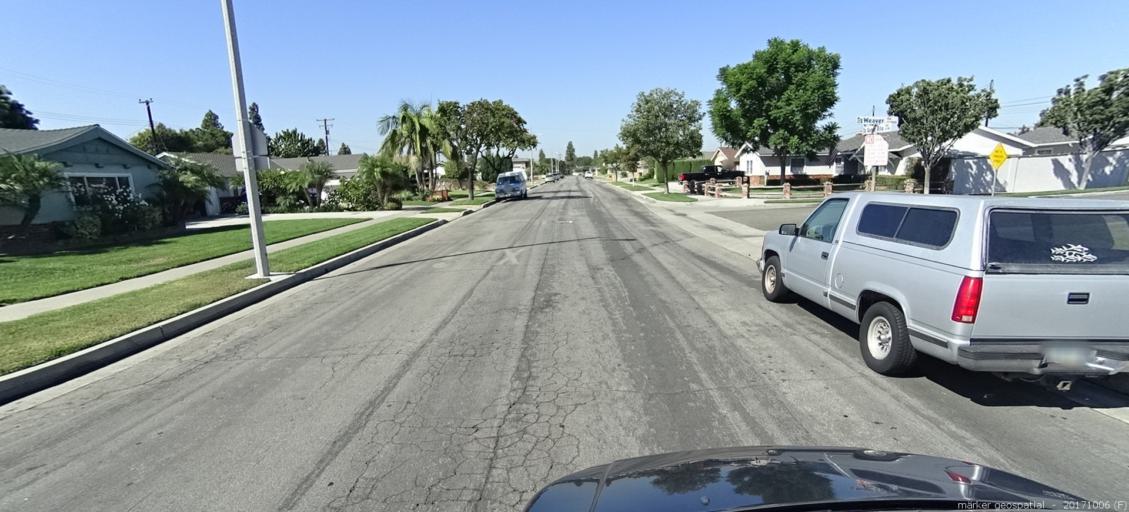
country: US
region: California
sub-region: Orange County
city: Stanton
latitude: 33.7893
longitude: -118.0160
